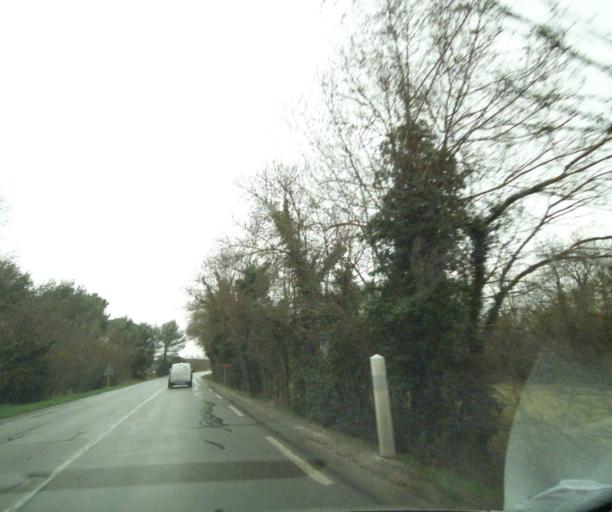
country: FR
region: Provence-Alpes-Cote d'Azur
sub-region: Departement des Bouches-du-Rhone
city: Lambesc
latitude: 43.6565
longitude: 5.2832
